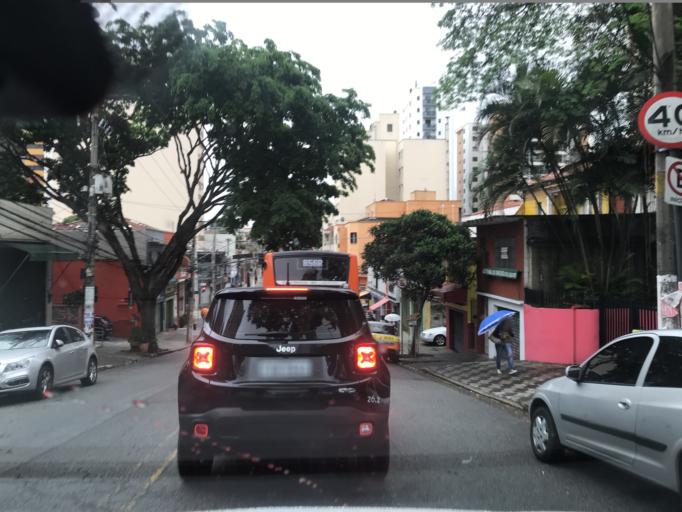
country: BR
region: Sao Paulo
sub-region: Sao Paulo
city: Sao Paulo
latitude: -23.5371
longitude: -46.6850
